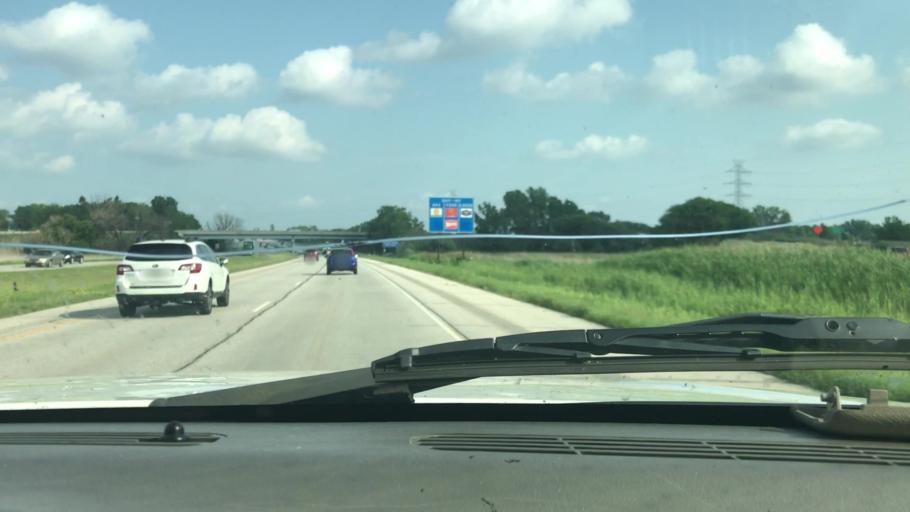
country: US
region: Wisconsin
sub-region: Brown County
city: Green Bay
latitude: 44.5415
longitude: -88.0277
